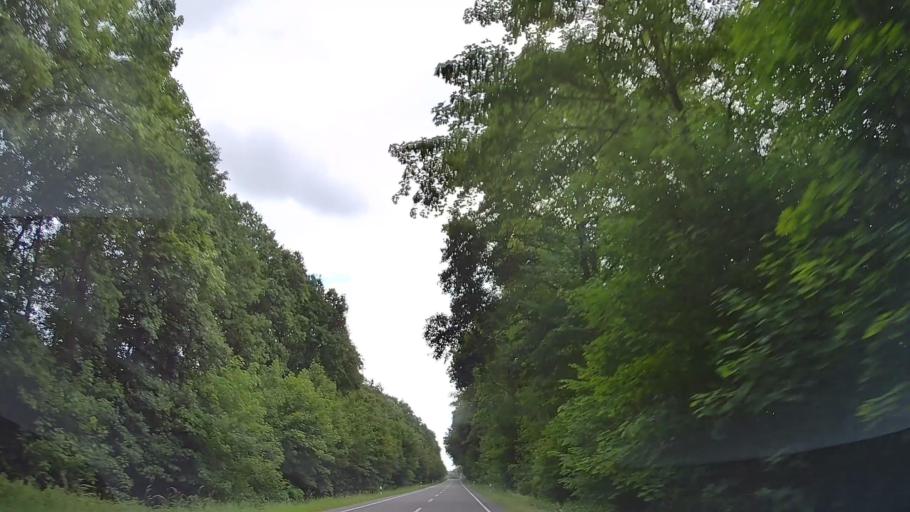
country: DE
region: Lower Saxony
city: Brockum
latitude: 52.4647
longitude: 8.4413
